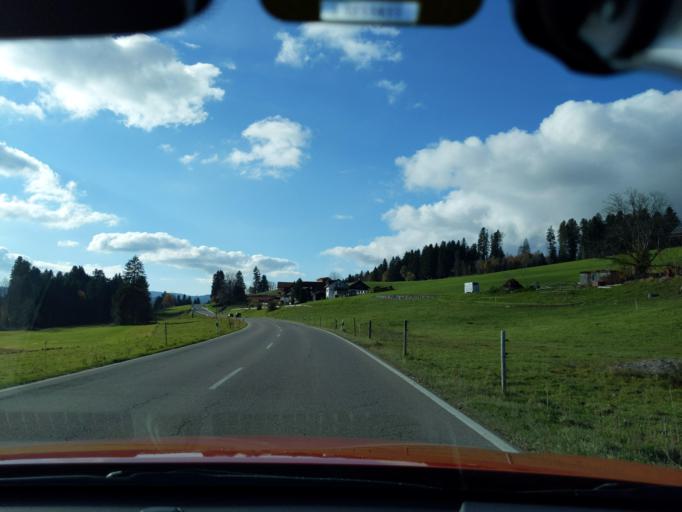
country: DE
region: Bavaria
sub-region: Swabia
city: Oberreute
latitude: 47.5691
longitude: 9.9391
